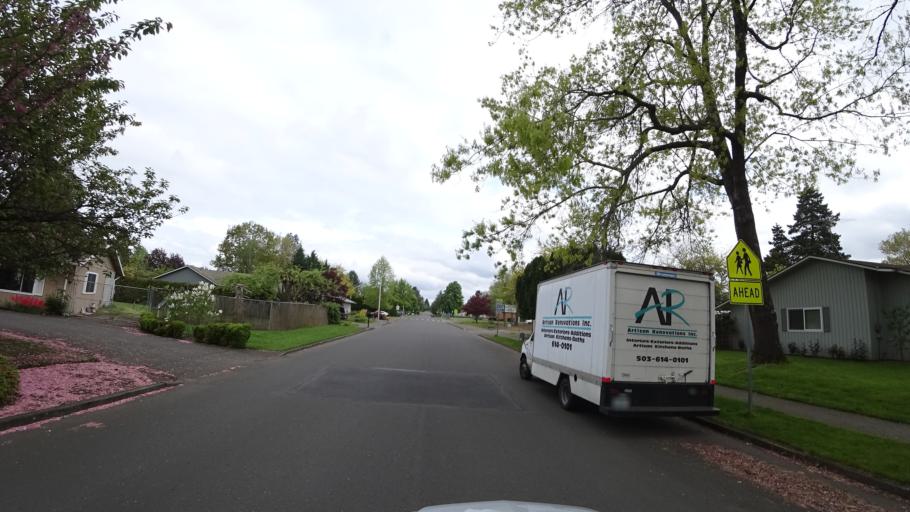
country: US
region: Oregon
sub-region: Washington County
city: Hillsboro
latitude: 45.5328
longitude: -122.9729
